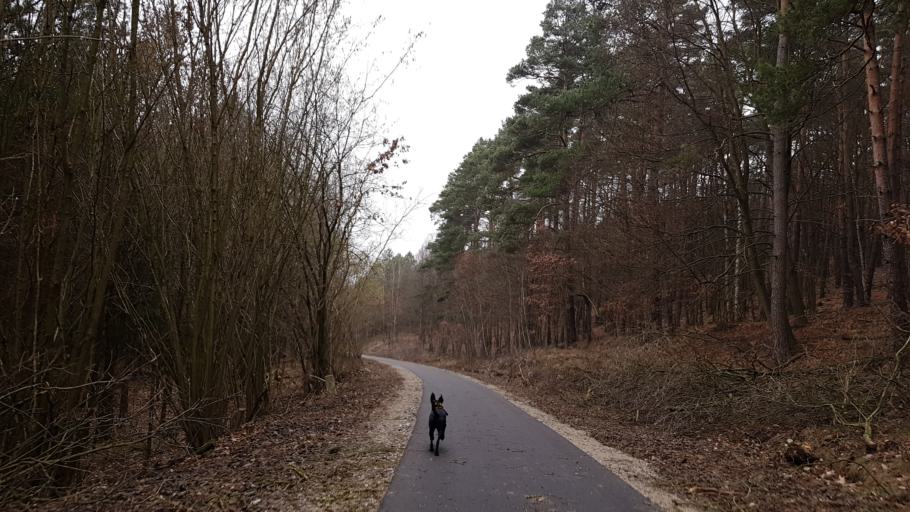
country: PL
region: West Pomeranian Voivodeship
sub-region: Powiat mysliborski
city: Barlinek
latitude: 53.0077
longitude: 15.2429
